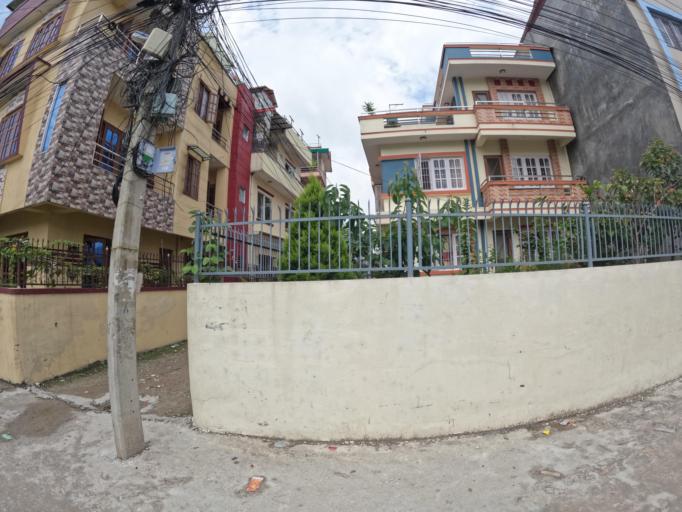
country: NP
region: Central Region
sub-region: Bagmati Zone
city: Kathmandu
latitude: 27.7599
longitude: 85.3179
